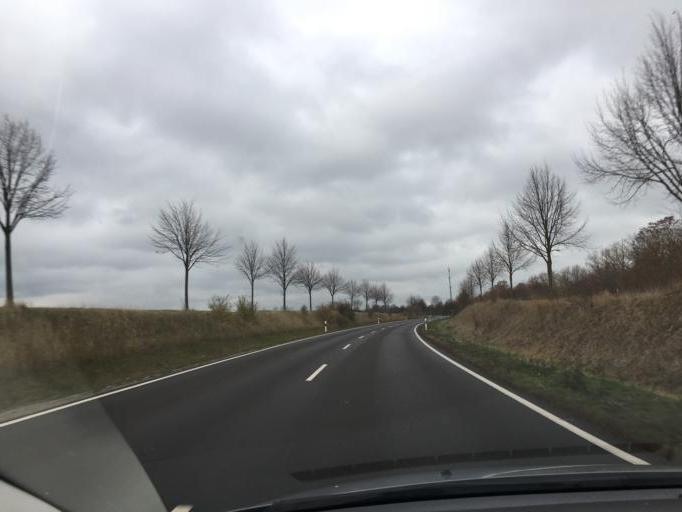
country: DE
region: Saxony-Anhalt
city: Wanzleben
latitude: 52.0540
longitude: 11.4471
